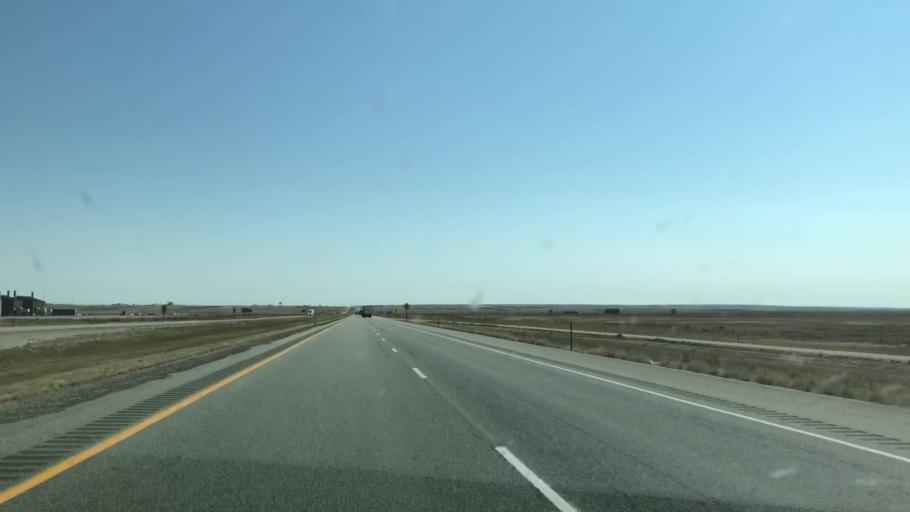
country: US
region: Wyoming
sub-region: Carbon County
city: Rawlins
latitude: 41.6655
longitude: -108.0299
